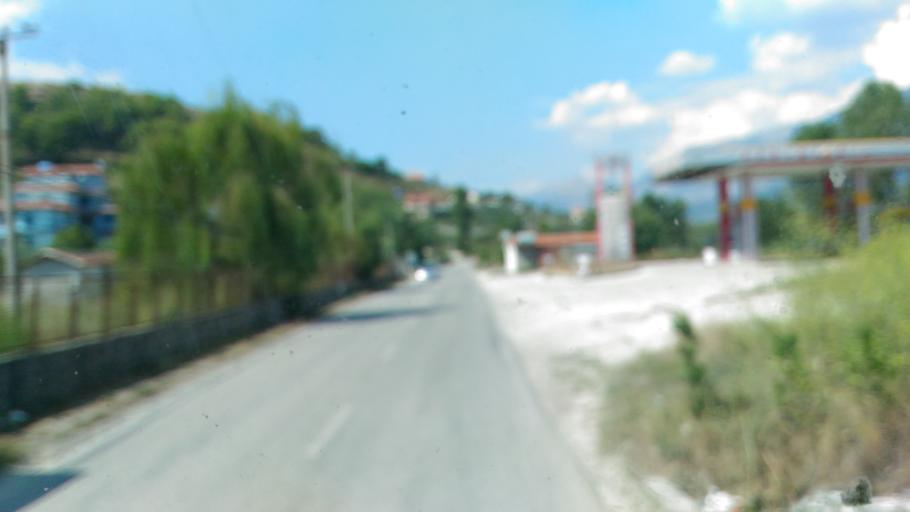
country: AL
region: Gjirokaster
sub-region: Rrethi i Gjirokastres
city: Dervician
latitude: 40.0578
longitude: 20.1727
